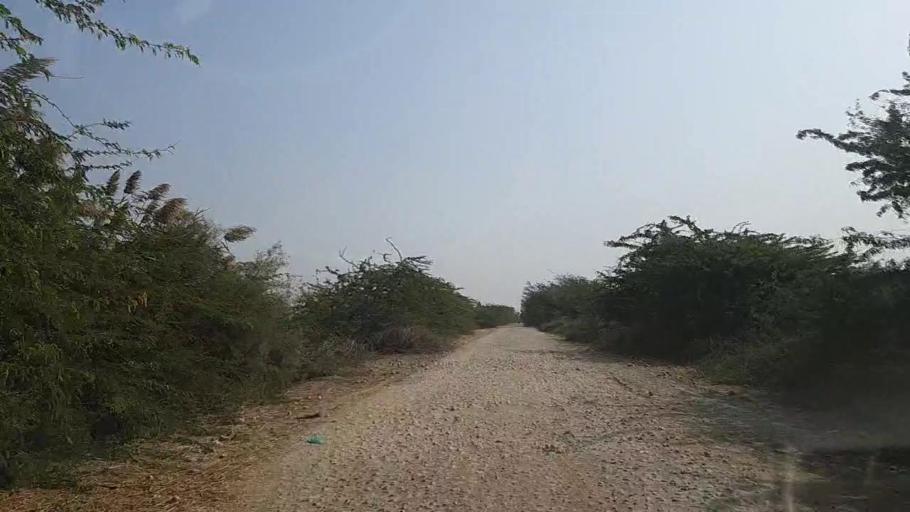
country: PK
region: Sindh
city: Keti Bandar
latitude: 24.2482
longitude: 67.6325
